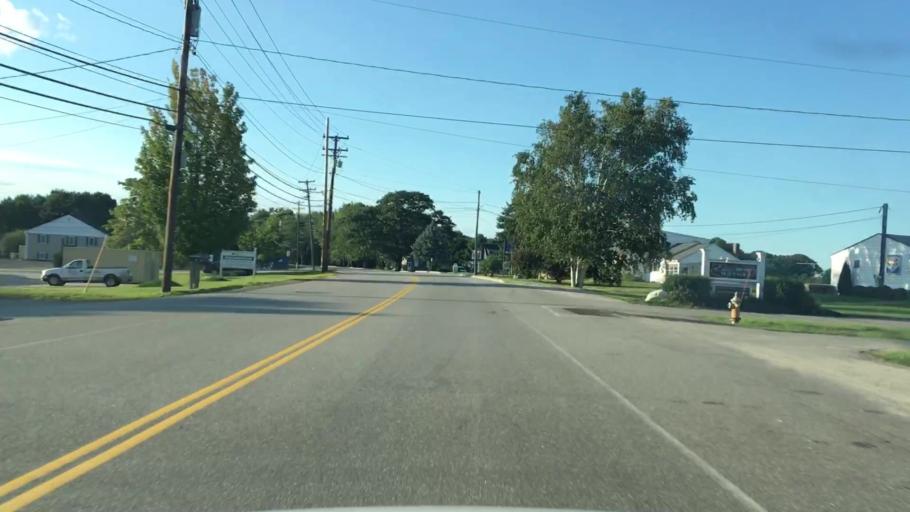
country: US
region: Maine
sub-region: Cumberland County
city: Scarborough
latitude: 43.5982
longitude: -70.2977
